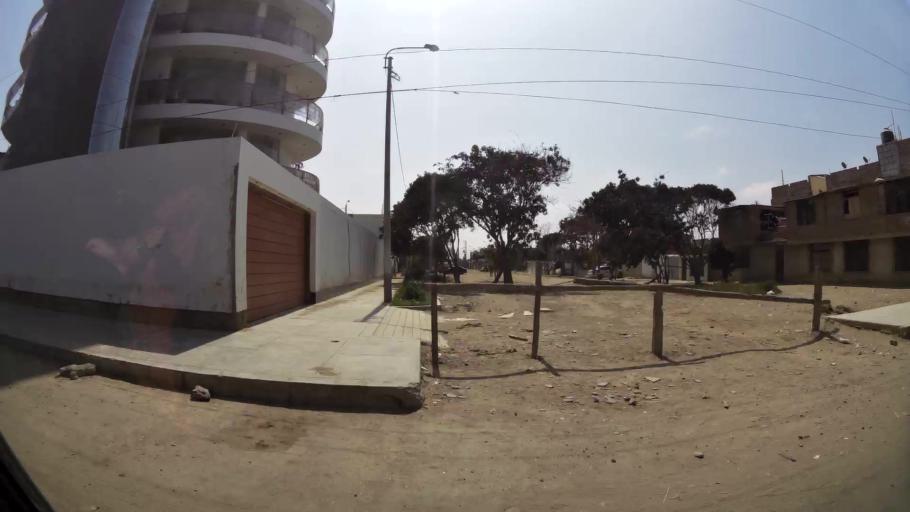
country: PE
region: La Libertad
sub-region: Provincia de Trujillo
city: Buenos Aires
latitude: -8.1258
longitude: -79.0460
